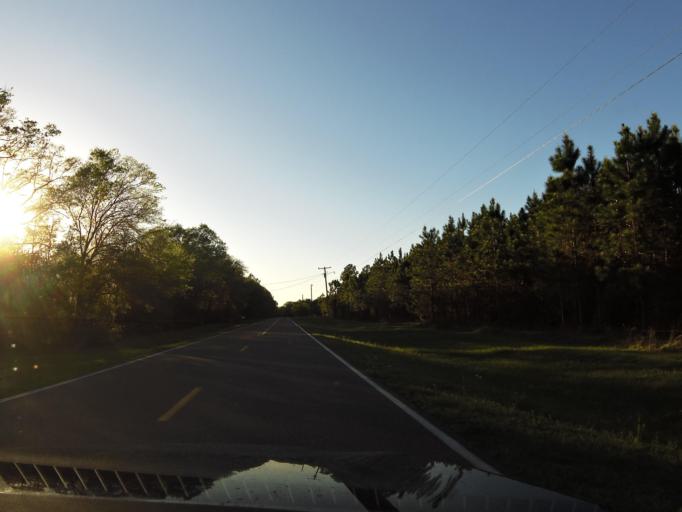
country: US
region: Florida
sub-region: Clay County
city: Keystone Heights
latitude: 29.8469
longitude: -82.0811
